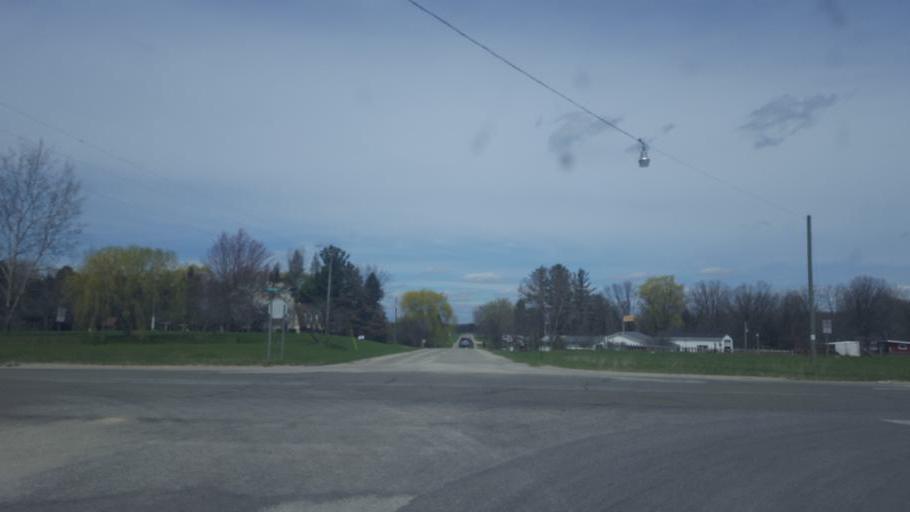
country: US
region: Michigan
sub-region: Isabella County
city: Lake Isabella
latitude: 43.5967
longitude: -84.9475
